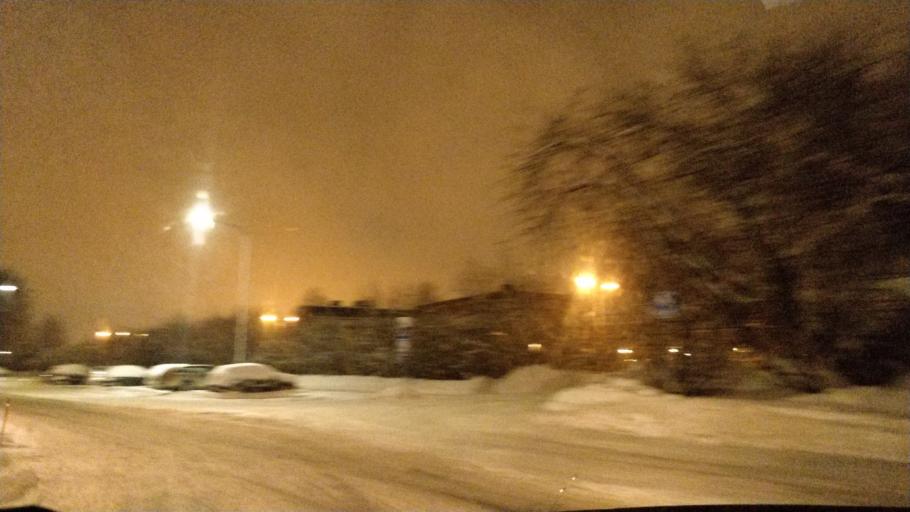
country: FI
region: Lapland
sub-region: Rovaniemi
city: Rovaniemi
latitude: 66.5011
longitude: 25.7219
